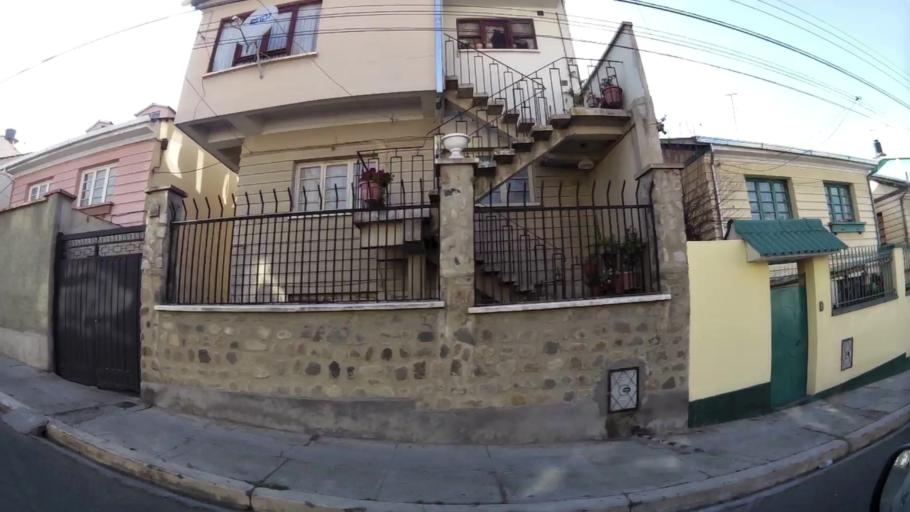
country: BO
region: La Paz
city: La Paz
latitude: -16.4901
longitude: -68.1236
